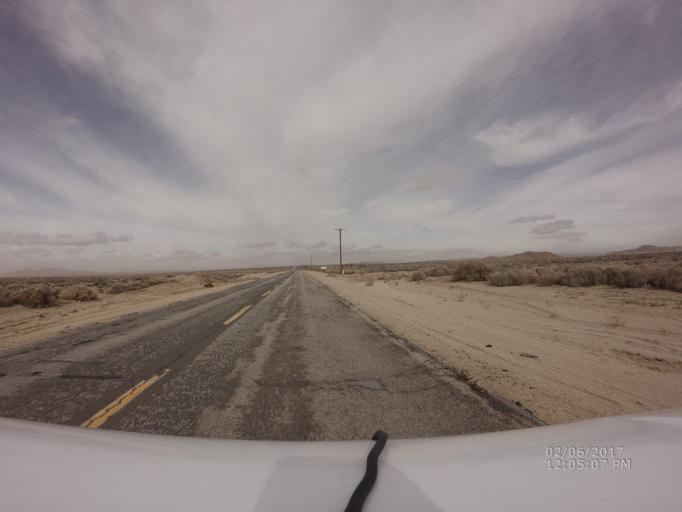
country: US
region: California
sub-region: Los Angeles County
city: Lake Los Angeles
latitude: 34.5964
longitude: -117.7024
